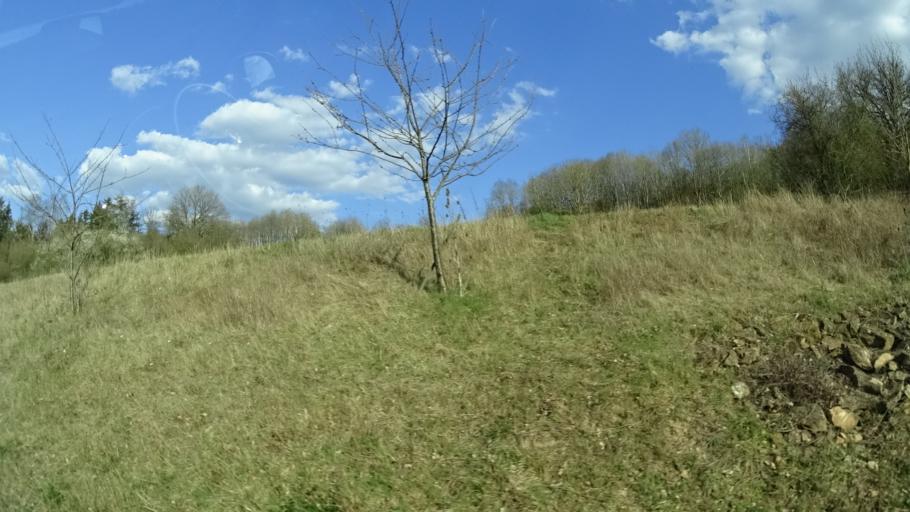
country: DE
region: Rheinland-Pfalz
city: Rehborn
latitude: 49.7296
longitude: 7.6769
